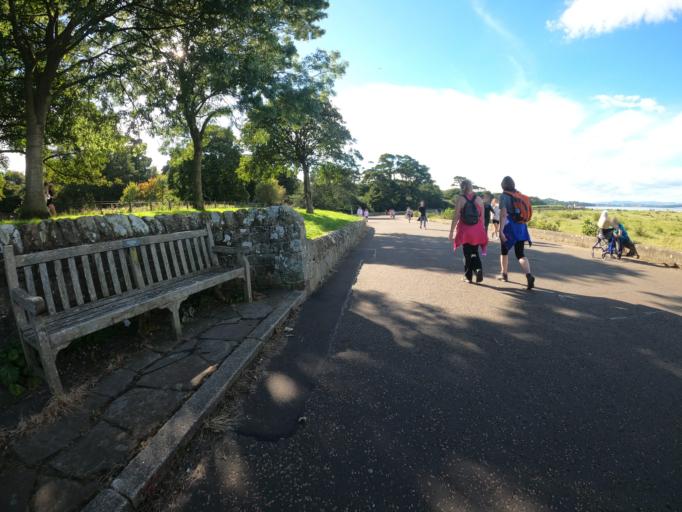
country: GB
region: Scotland
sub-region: Fife
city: Aberdour
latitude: 55.9796
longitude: -3.2964
